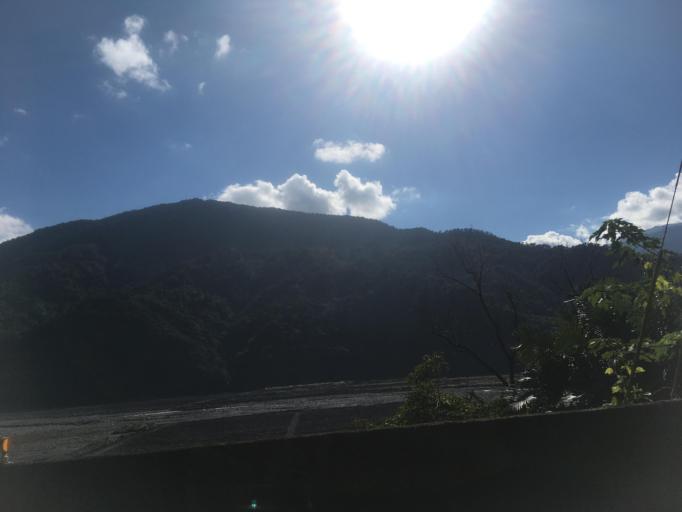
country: TW
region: Taiwan
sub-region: Yilan
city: Yilan
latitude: 24.5878
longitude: 121.5033
